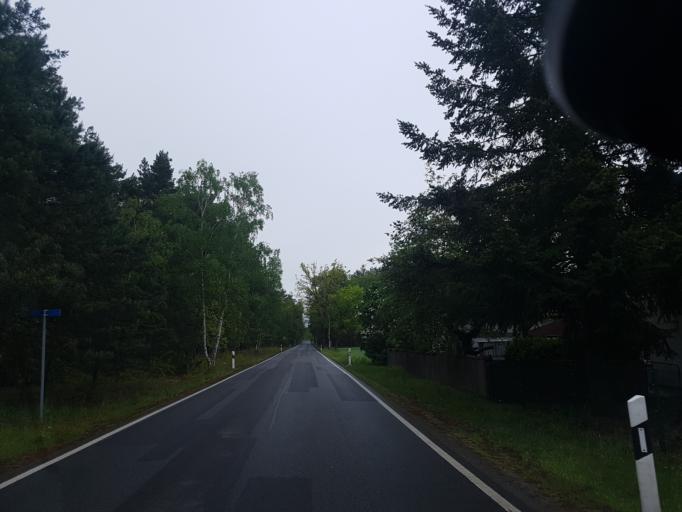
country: DE
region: Brandenburg
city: Spremberg
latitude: 51.6603
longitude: 14.4420
